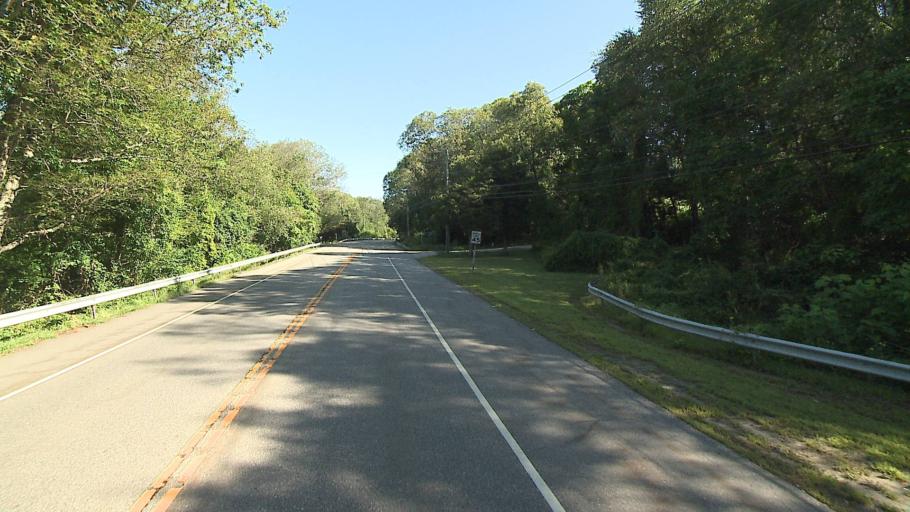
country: US
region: Connecticut
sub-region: New London County
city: Gales Ferry
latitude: 41.4457
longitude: -72.0769
